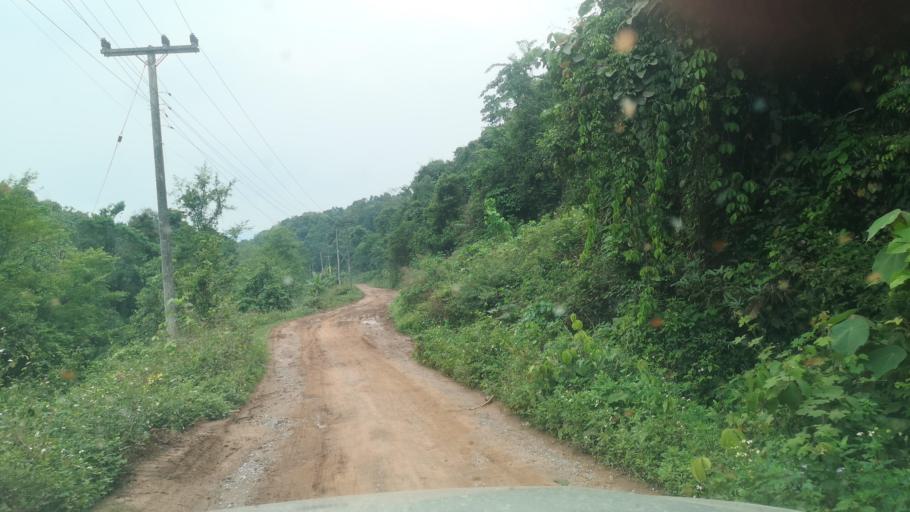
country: LA
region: Oudomxai
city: Muang La
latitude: 21.0733
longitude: 101.8399
